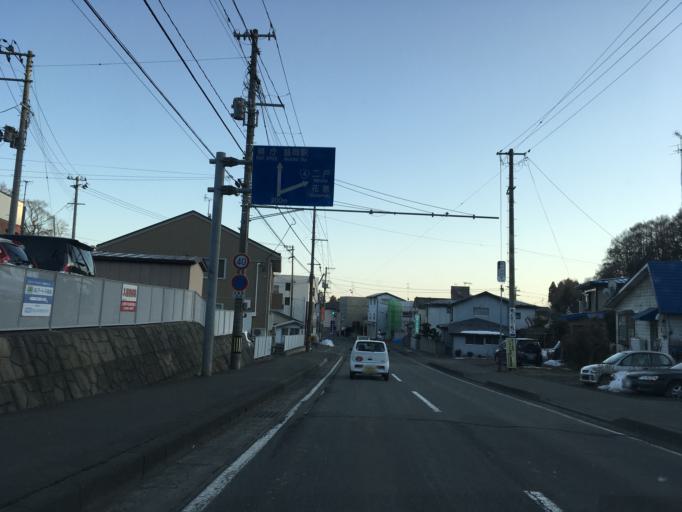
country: JP
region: Iwate
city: Morioka-shi
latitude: 39.7182
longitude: 141.1547
